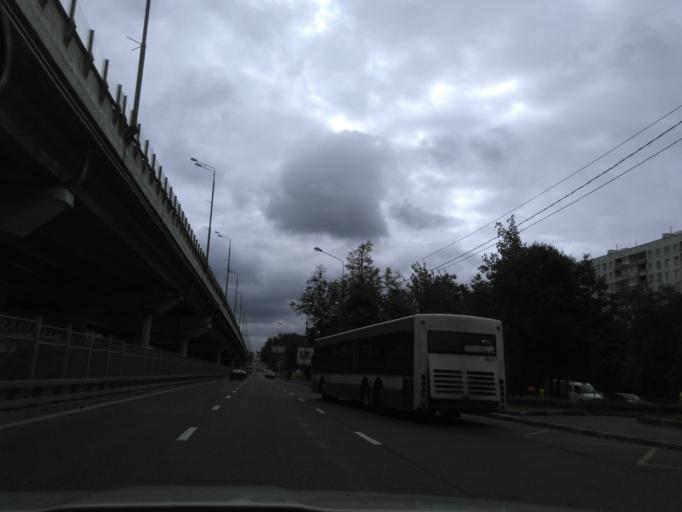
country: RU
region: Moskovskaya
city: Bol'shaya Setun'
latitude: 55.7519
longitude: 37.4068
